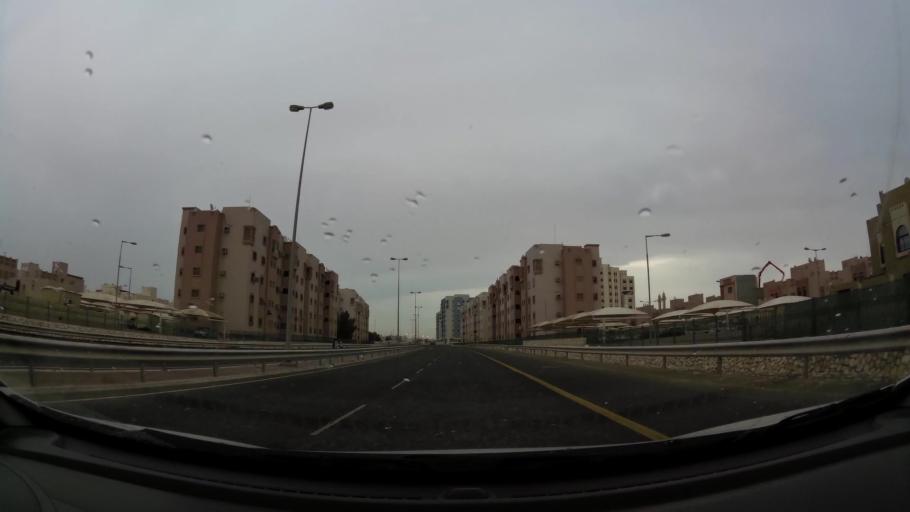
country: BH
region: Central Governorate
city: Madinat Hamad
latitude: 26.1182
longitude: 50.4886
